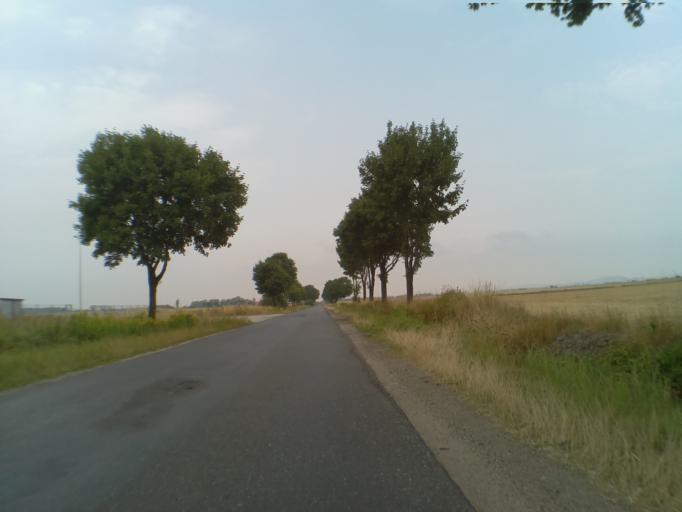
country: PL
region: Lower Silesian Voivodeship
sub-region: Powiat swidnicki
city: Swiebodzice
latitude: 50.8785
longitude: 16.3302
